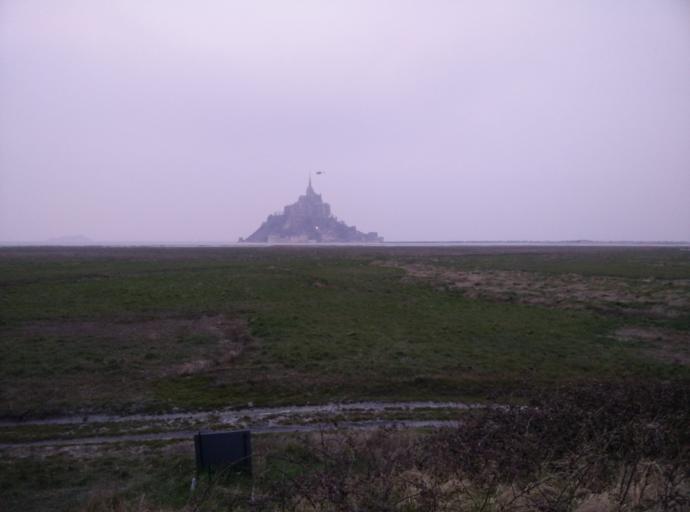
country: FR
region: Lower Normandy
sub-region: Departement de la Manche
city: Pontorson
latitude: 48.6271
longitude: -1.5188
